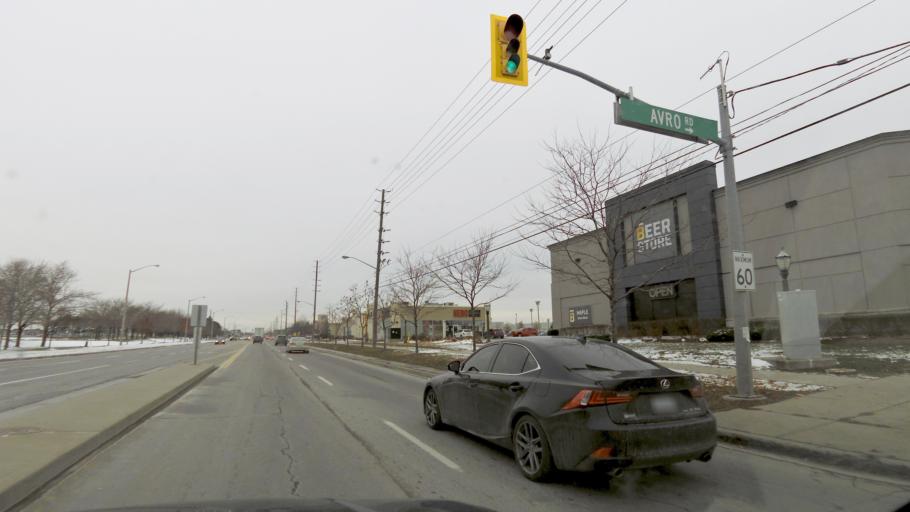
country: CA
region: Ontario
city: Vaughan
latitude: 43.8462
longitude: -79.5359
